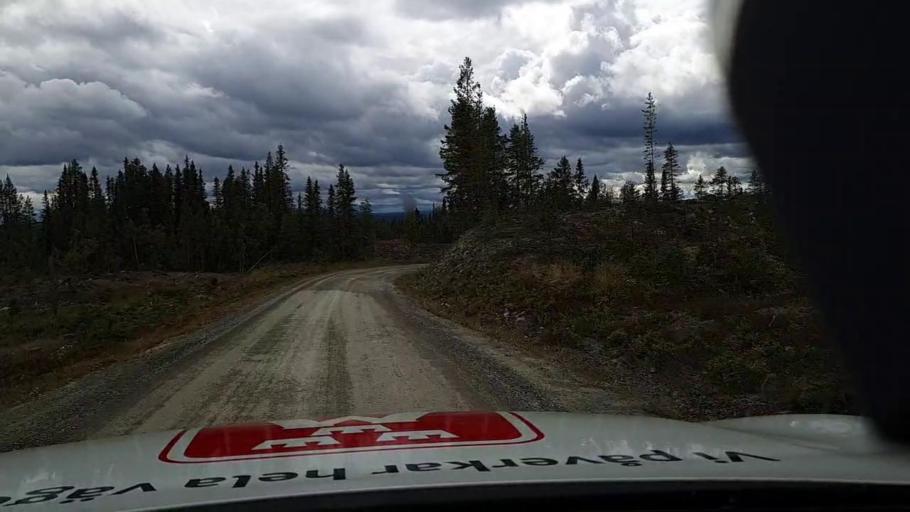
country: SE
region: Jaemtland
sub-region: Are Kommun
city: Jarpen
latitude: 62.8111
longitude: 13.8087
